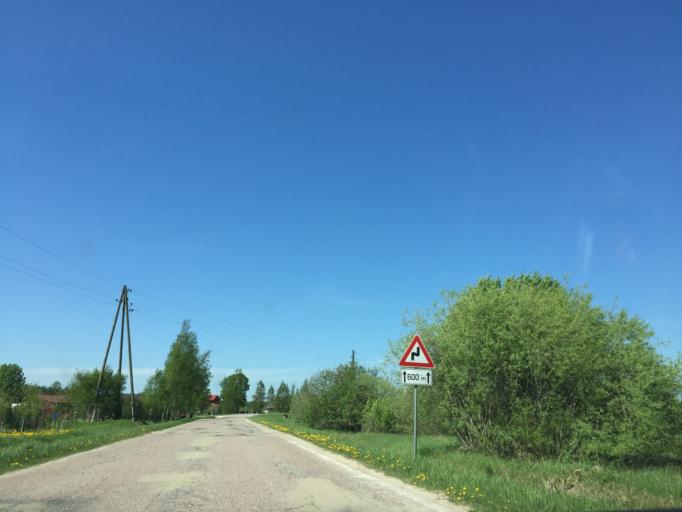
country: LV
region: Ogre
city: Ogre
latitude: 56.8525
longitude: 24.7116
